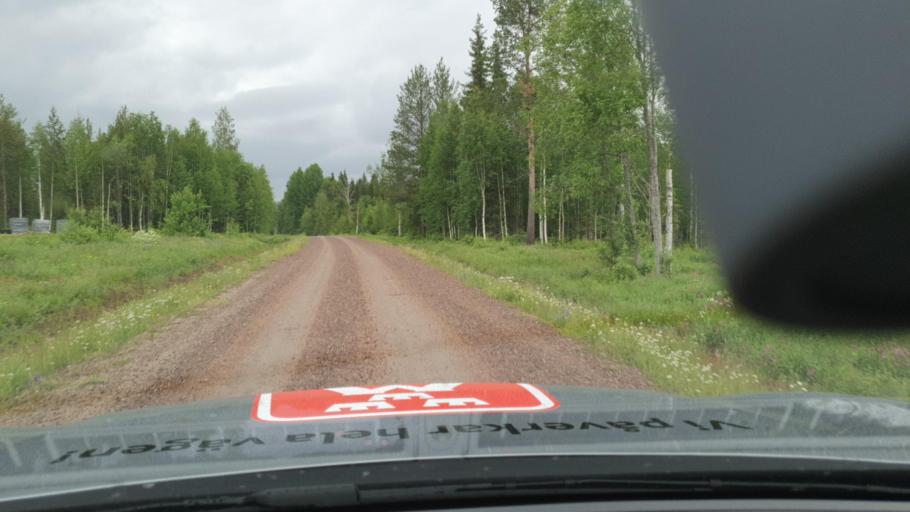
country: SE
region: Norrbotten
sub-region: Overkalix Kommun
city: OEverkalix
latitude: 66.6065
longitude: 22.7464
